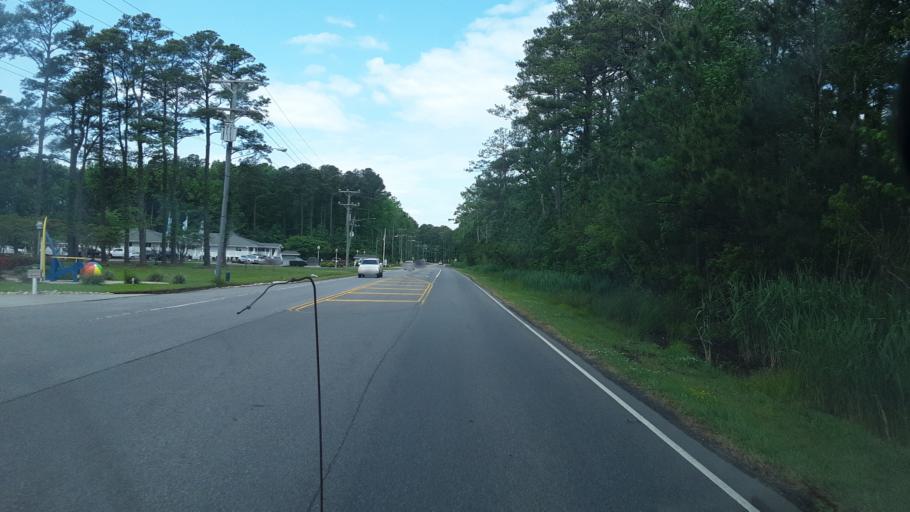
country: US
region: Virginia
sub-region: City of Virginia Beach
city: Virginia Beach
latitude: 36.7432
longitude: -75.9566
